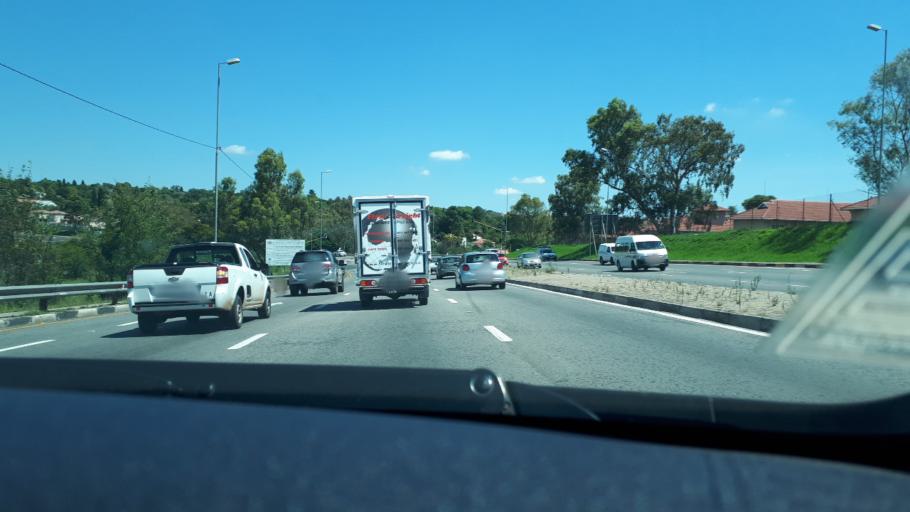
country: ZA
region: Gauteng
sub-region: City of Johannesburg Metropolitan Municipality
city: Roodepoort
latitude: -26.0712
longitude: 27.9732
